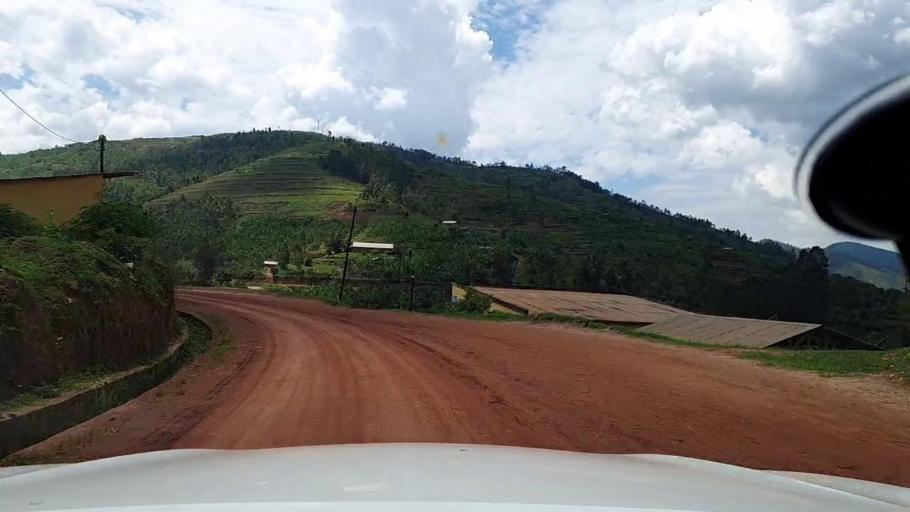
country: RW
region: Northern Province
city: Musanze
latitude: -1.6903
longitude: 29.8215
